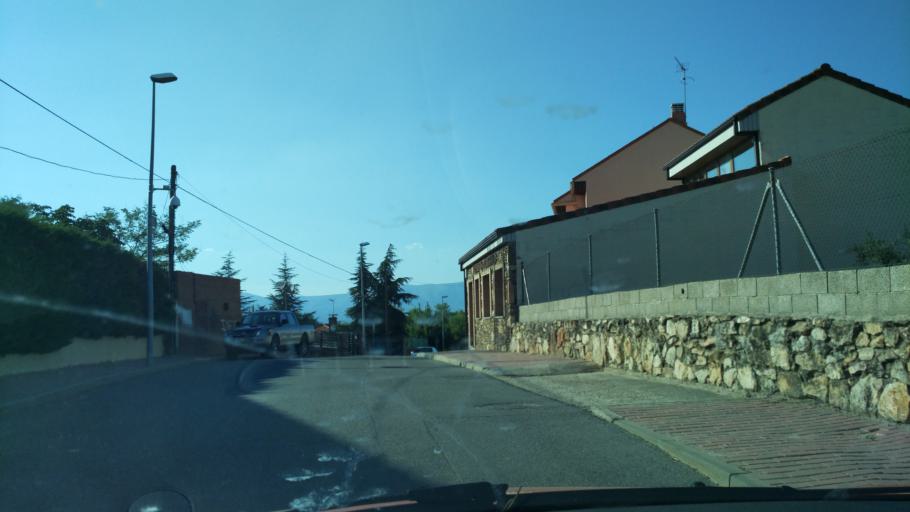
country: ES
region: Madrid
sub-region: Provincia de Madrid
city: Pedrezuela
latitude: 40.7431
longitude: -3.5977
